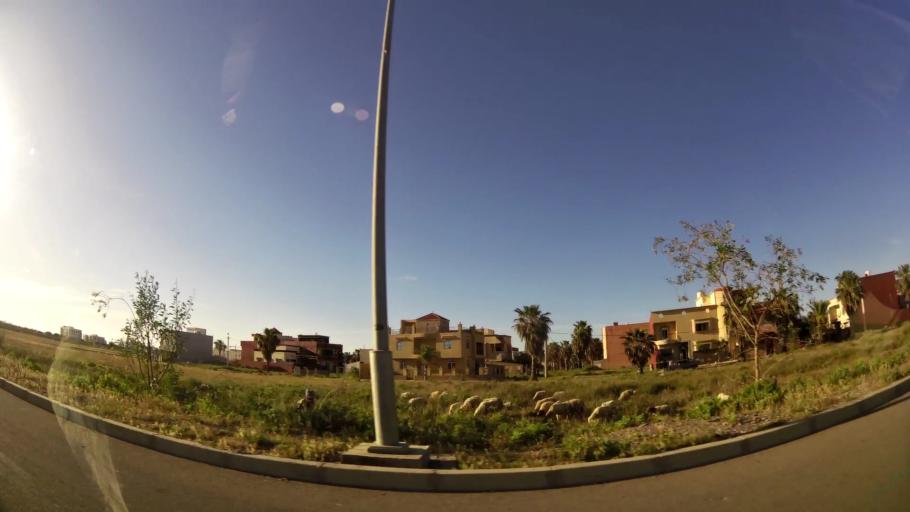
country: MA
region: Oriental
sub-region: Berkane-Taourirt
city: Madagh
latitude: 35.0818
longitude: -2.2499
